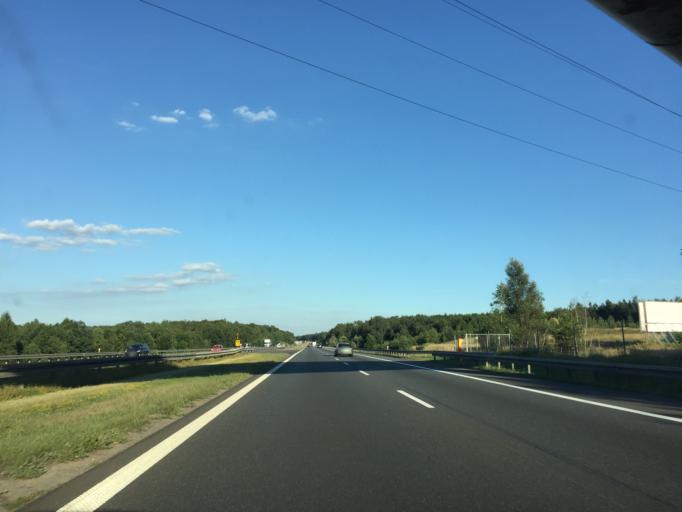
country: PL
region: Silesian Voivodeship
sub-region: Katowice
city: Murcki
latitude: 50.2272
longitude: 19.0789
